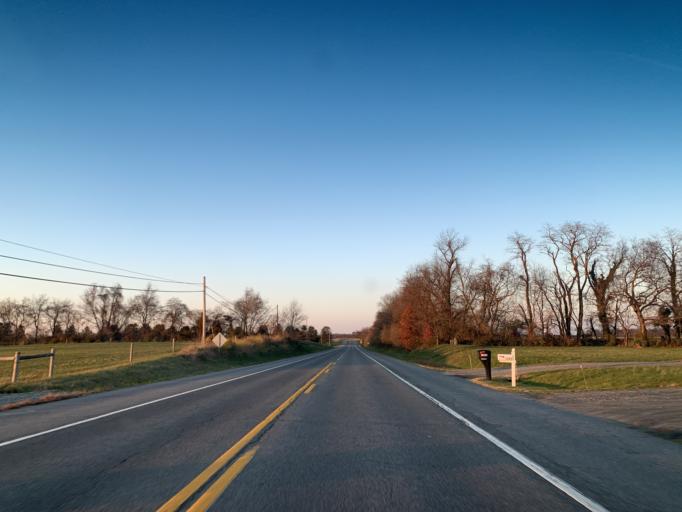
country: US
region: Maryland
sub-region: Cecil County
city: Charlestown
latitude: 39.4178
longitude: -75.9179
